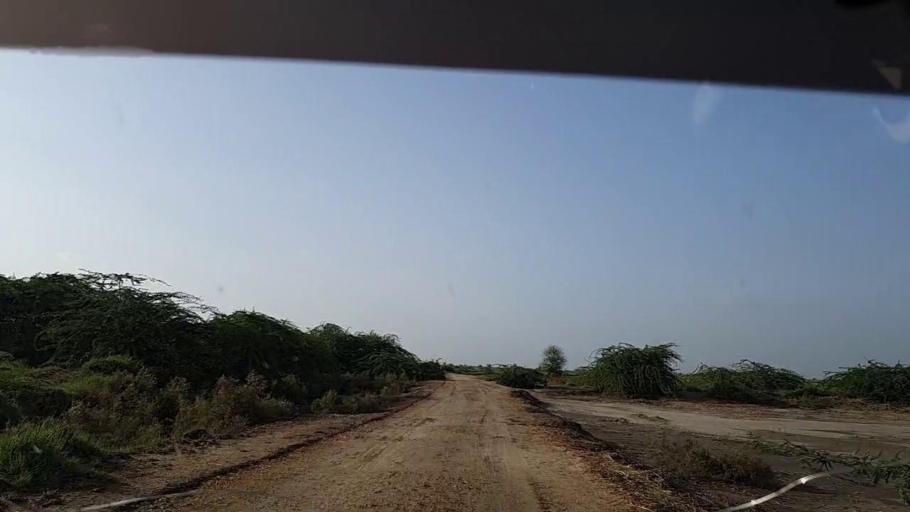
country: PK
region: Sindh
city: Badin
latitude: 24.5684
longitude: 68.8795
